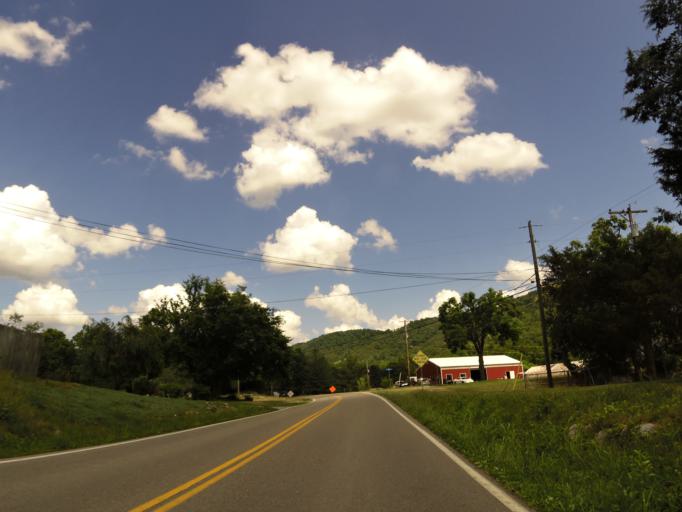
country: US
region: Virginia
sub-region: Lee County
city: Pennington Gap
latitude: 36.7038
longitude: -82.9789
